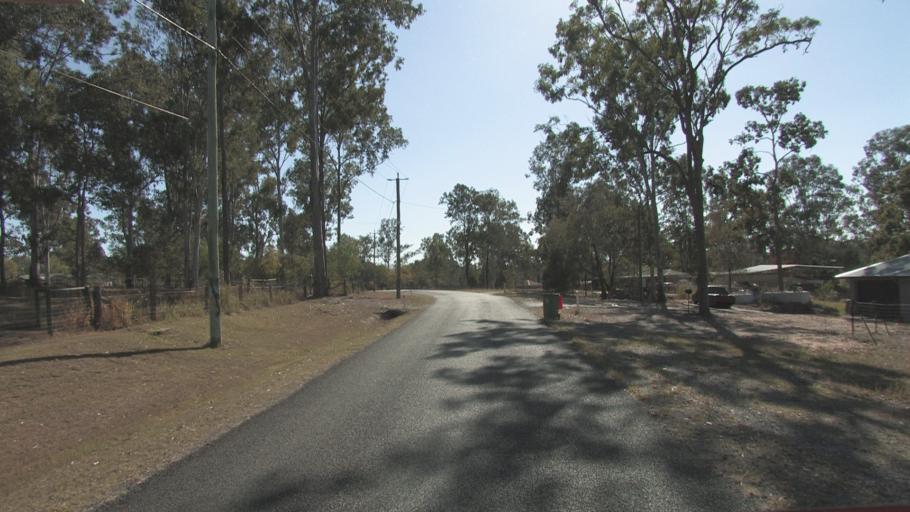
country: AU
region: Queensland
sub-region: Logan
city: North Maclean
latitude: -27.8240
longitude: 153.0456
